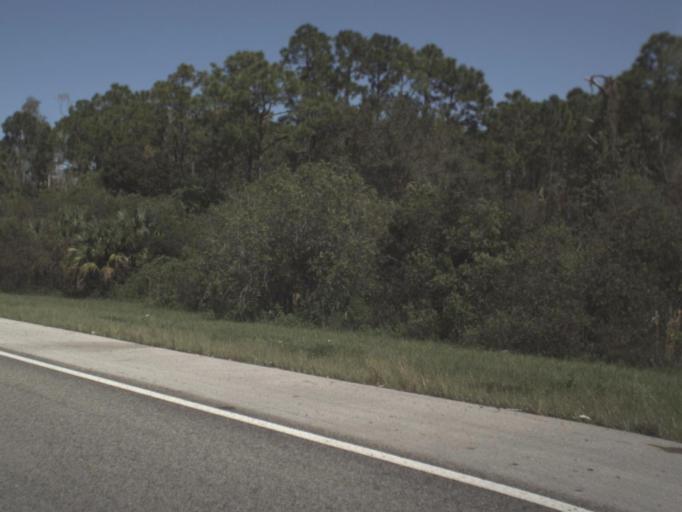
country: US
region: Florida
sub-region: Lee County
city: Tice
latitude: 26.6408
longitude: -81.8009
